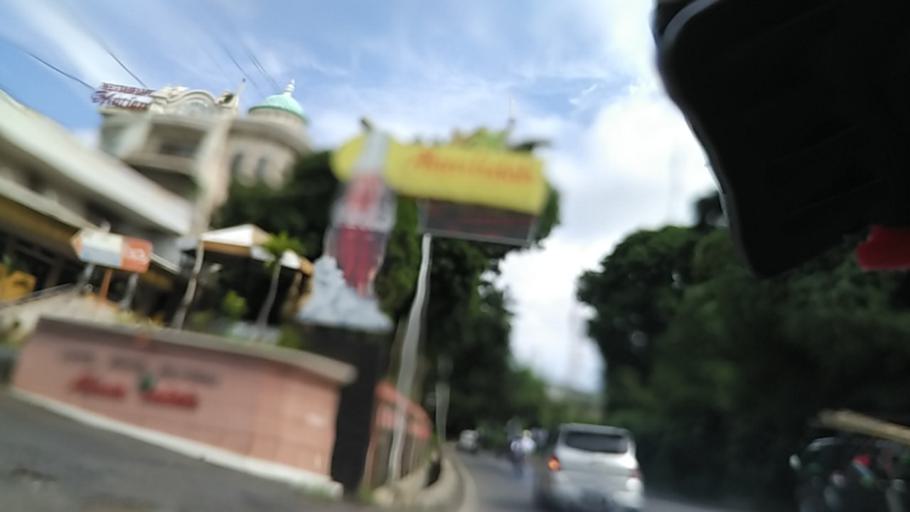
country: ID
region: Central Java
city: Semarang
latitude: -7.0402
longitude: 110.4214
